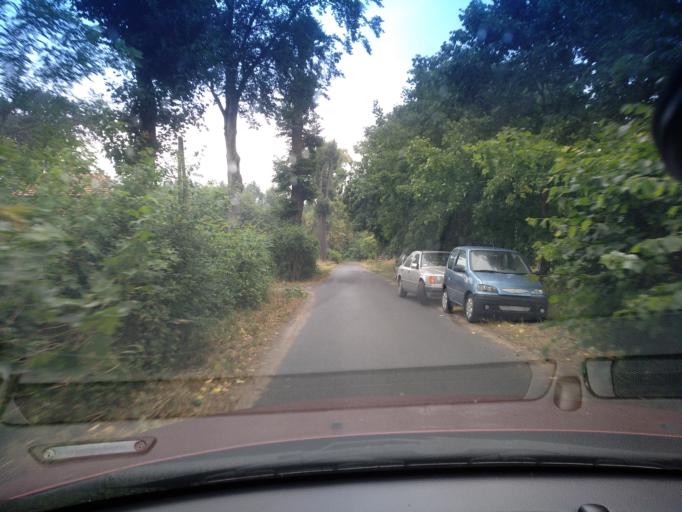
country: PL
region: Lower Silesian Voivodeship
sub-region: Powiat zgorzelecki
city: Wegliniec
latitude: 51.2649
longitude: 15.1965
